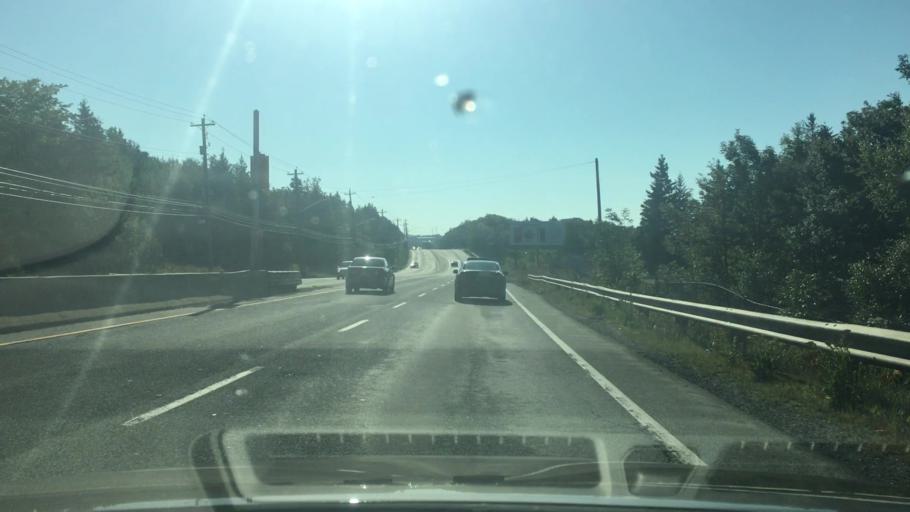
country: CA
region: Nova Scotia
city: Dartmouth
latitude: 44.7067
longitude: -63.6200
